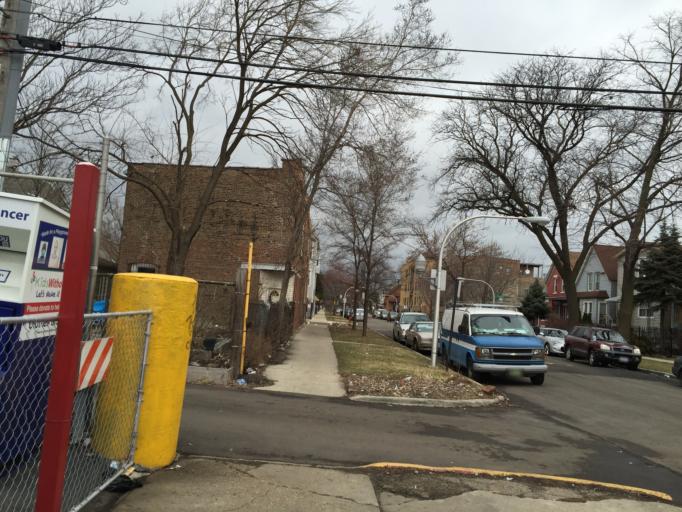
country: US
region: Illinois
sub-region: Cook County
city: Oak Park
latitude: 41.9104
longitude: -87.7191
